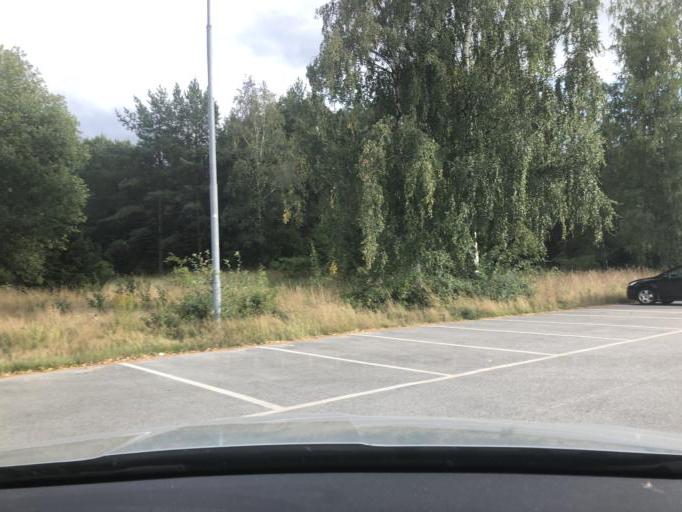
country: SE
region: Stockholm
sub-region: Botkyrka Kommun
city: Tullinge
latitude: 59.2191
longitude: 17.9310
